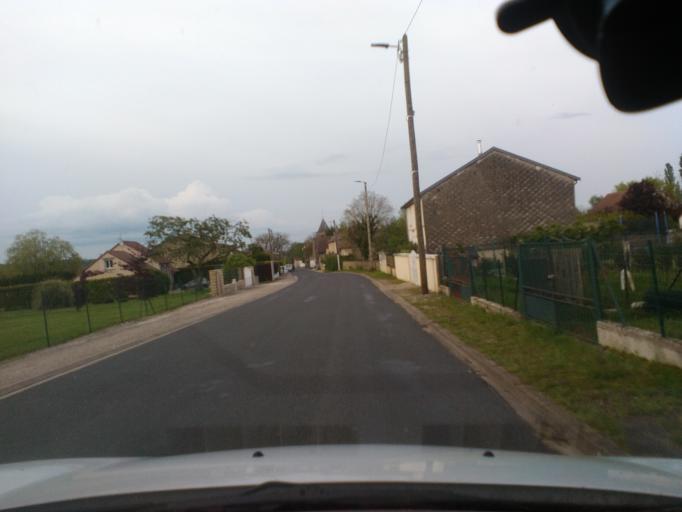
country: FR
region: Champagne-Ardenne
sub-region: Departement de la Haute-Marne
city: Doulaincourt-Saucourt
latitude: 48.2221
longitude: 5.2572
